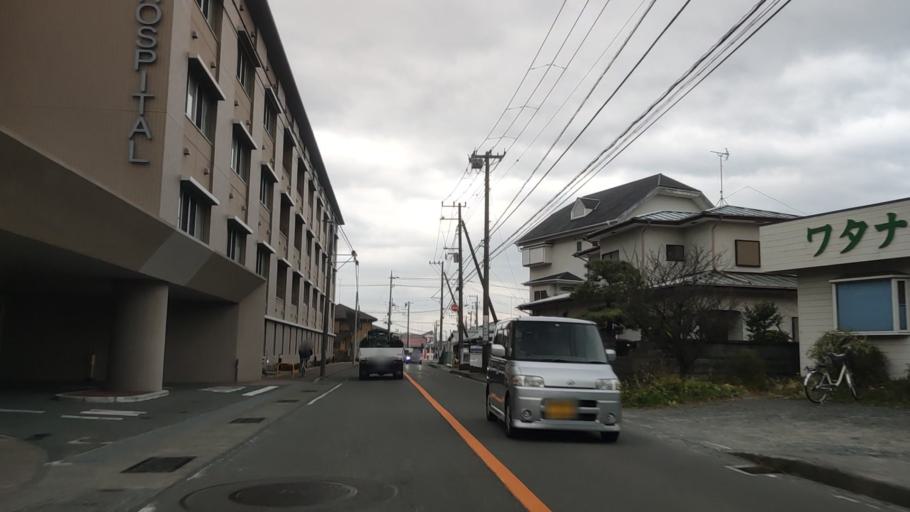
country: JP
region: Kanagawa
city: Odawara
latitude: 35.2832
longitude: 139.1977
